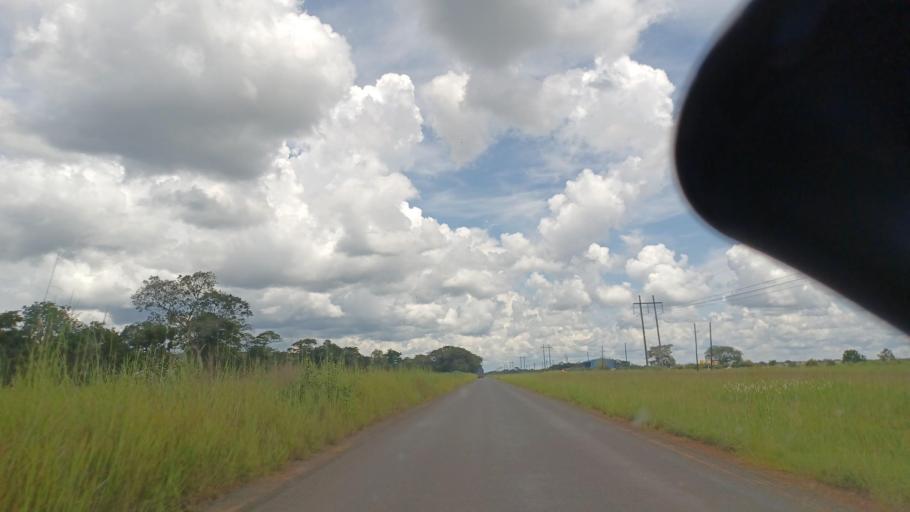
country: ZM
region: North-Western
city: Solwezi
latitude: -12.4440
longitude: 26.2079
